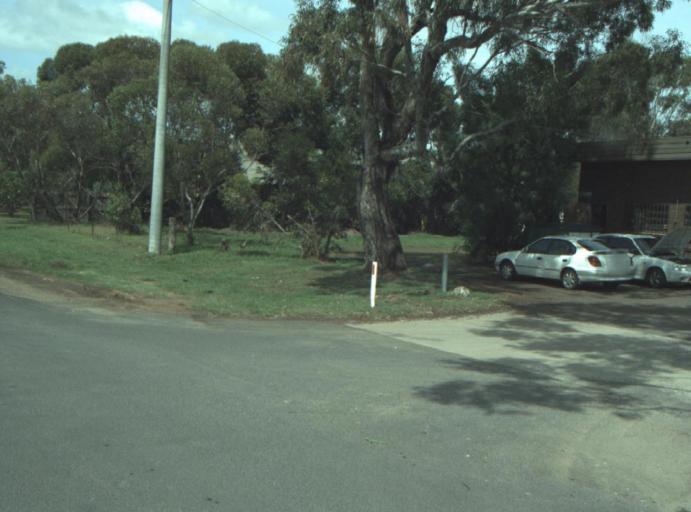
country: AU
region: Victoria
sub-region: Wyndham
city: Little River
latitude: -37.9620
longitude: 144.5080
